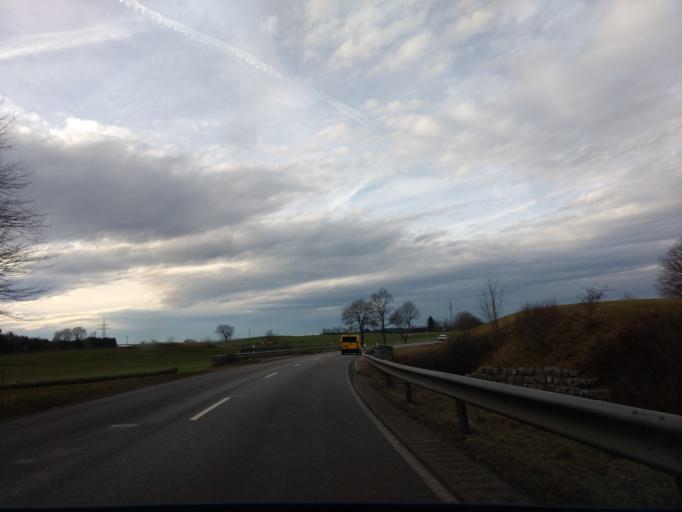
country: DE
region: Bavaria
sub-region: Upper Bavaria
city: Vachendorf
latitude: 47.8704
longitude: 12.6059
